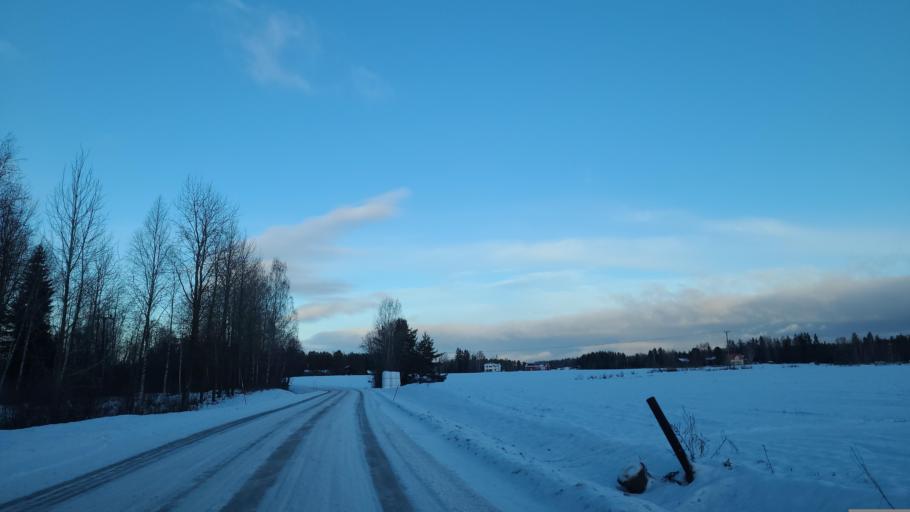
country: SE
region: Gaevleborg
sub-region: Bollnas Kommun
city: Bollnas
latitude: 61.3784
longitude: 16.4030
